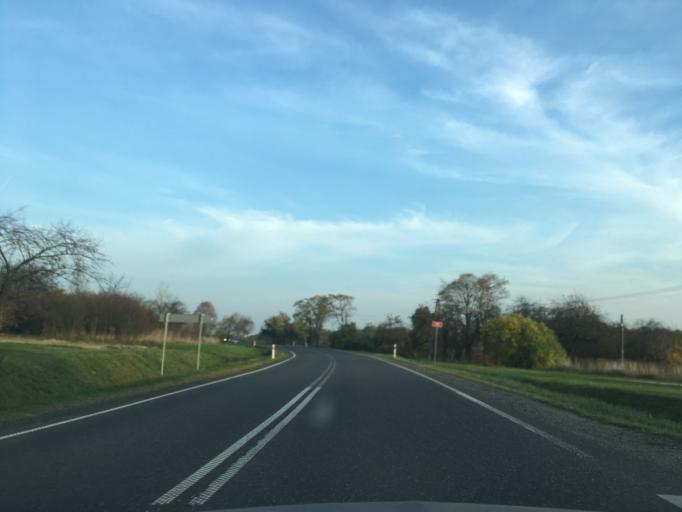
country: PL
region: Lodz Voivodeship
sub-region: Powiat skierniewicki
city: Kowiesy
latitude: 51.9198
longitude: 20.4327
